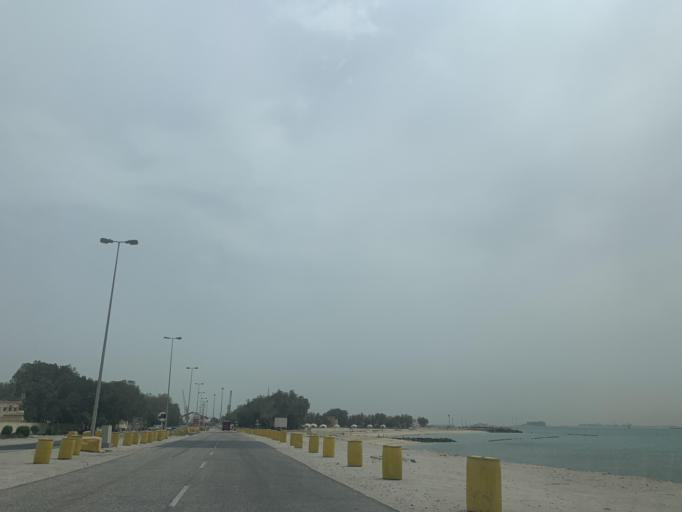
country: BH
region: Muharraq
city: Al Hadd
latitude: 26.1994
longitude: 50.6619
